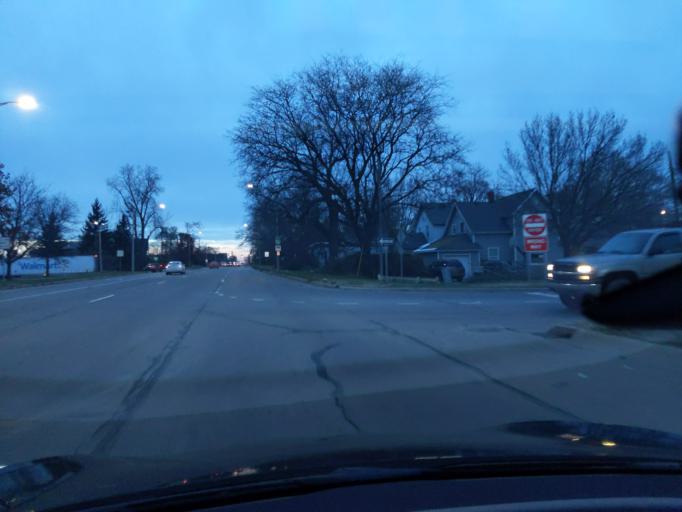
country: US
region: Michigan
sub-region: Ingham County
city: Lansing
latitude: 42.7270
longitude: -84.5447
